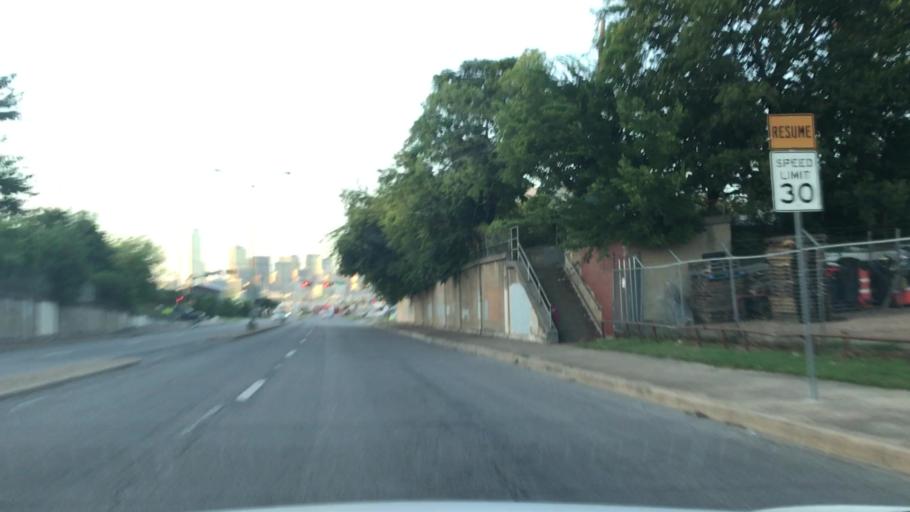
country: US
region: Texas
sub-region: Dallas County
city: Dallas
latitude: 32.7502
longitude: -96.8120
